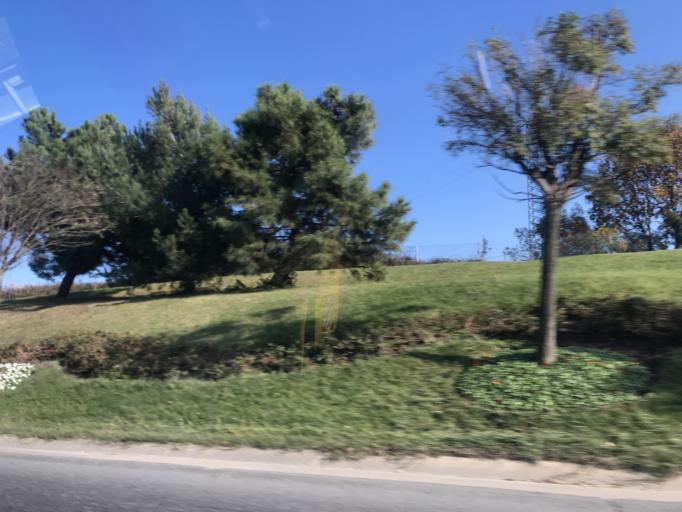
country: TR
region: Istanbul
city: Sultanbeyli
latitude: 40.9376
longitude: 29.3325
